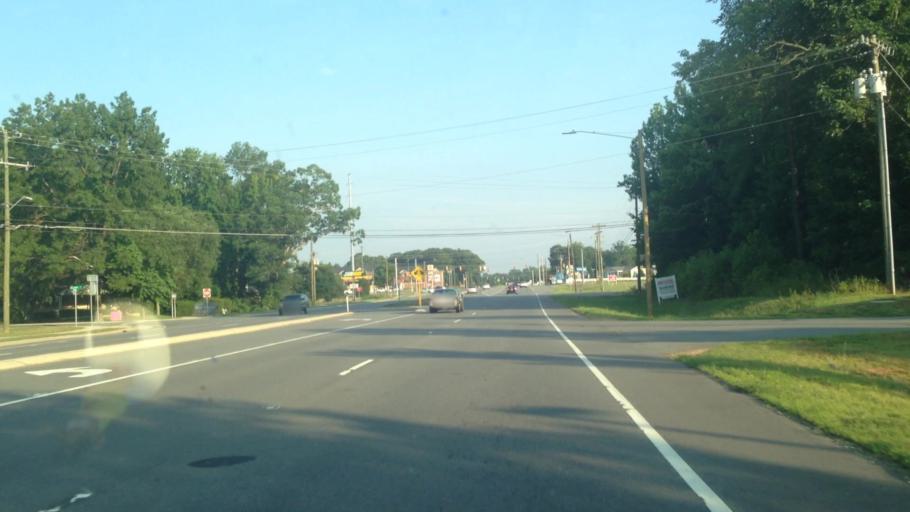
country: US
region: North Carolina
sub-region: Rockingham County
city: Reidsville
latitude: 36.3274
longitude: -79.6884
